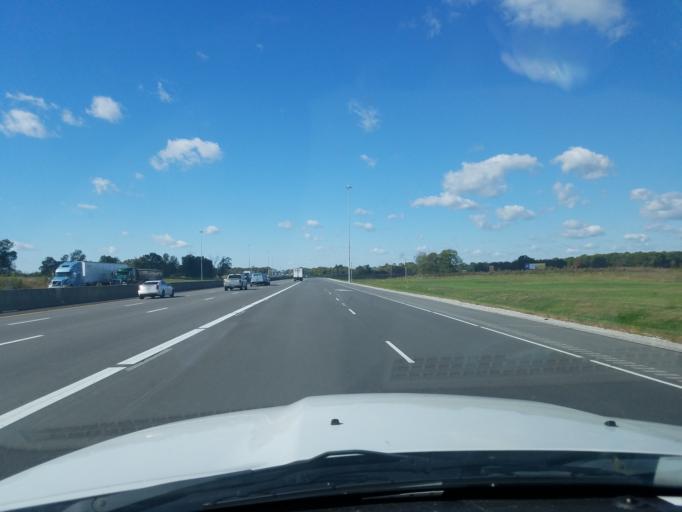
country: US
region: Kentucky
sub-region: Warren County
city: Bowling Green
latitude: 37.0119
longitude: -86.3308
